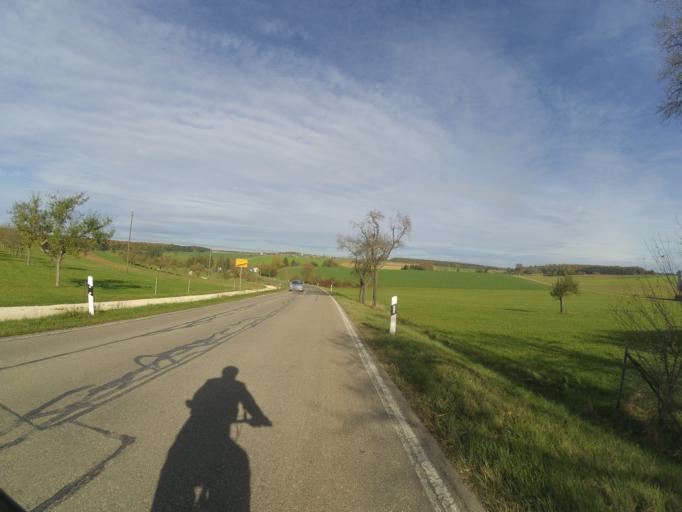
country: DE
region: Baden-Wuerttemberg
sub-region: Tuebingen Region
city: Lonsee
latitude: 48.5664
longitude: 9.9241
